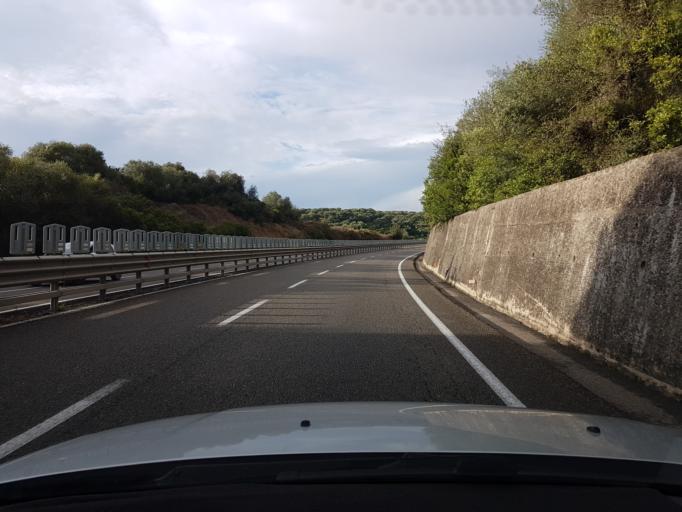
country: IT
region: Sardinia
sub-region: Provincia di Oristano
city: Bauladu
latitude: 40.0495
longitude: 8.7087
